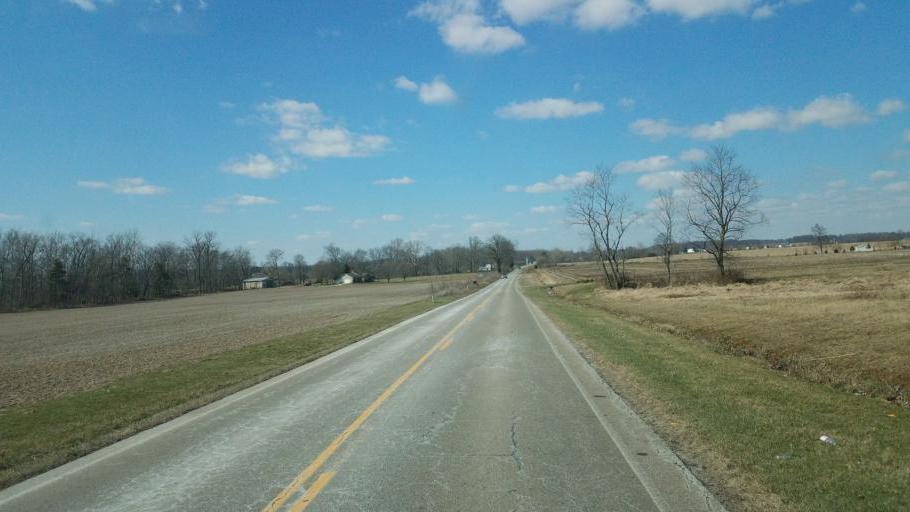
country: US
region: Ohio
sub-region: Knox County
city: Mount Vernon
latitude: 40.4247
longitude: -82.4992
